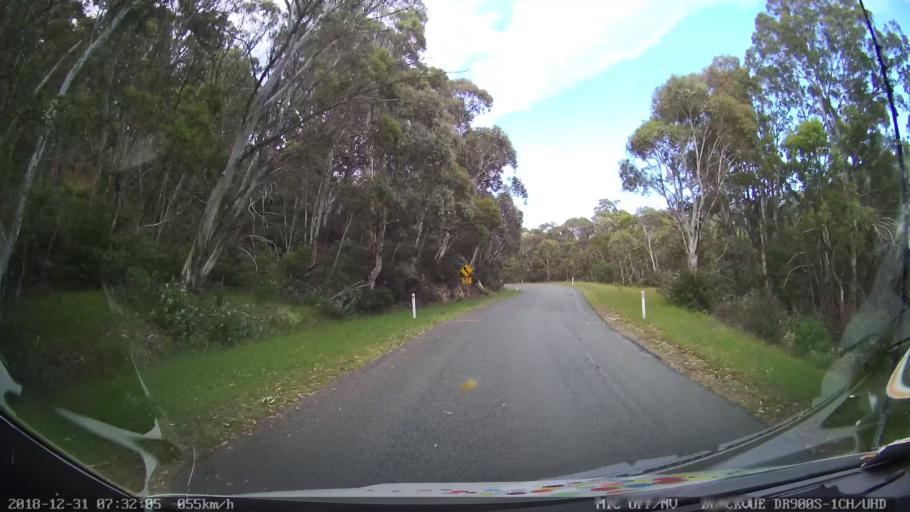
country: AU
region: New South Wales
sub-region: Snowy River
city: Jindabyne
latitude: -36.3294
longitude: 148.4680
